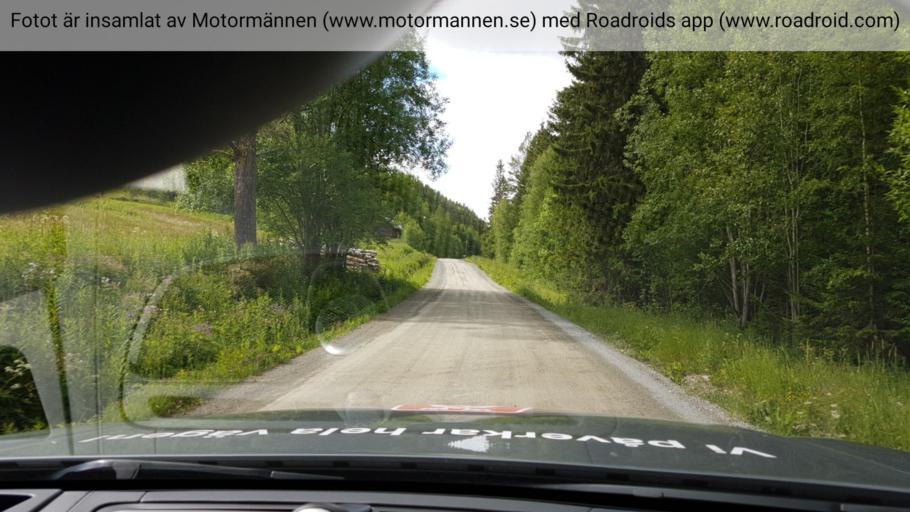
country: SE
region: Jaemtland
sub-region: Bergs Kommun
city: Hoverberg
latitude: 62.9234
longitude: 14.3040
